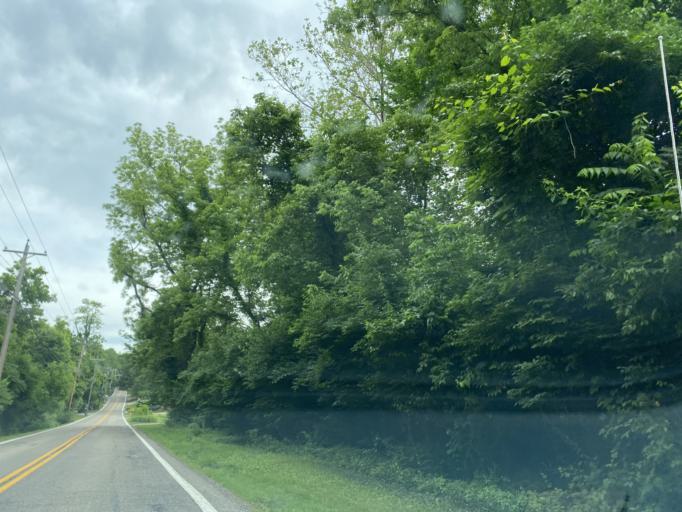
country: US
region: Ohio
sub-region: Hamilton County
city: Salem Heights
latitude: 39.0847
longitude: -84.4072
